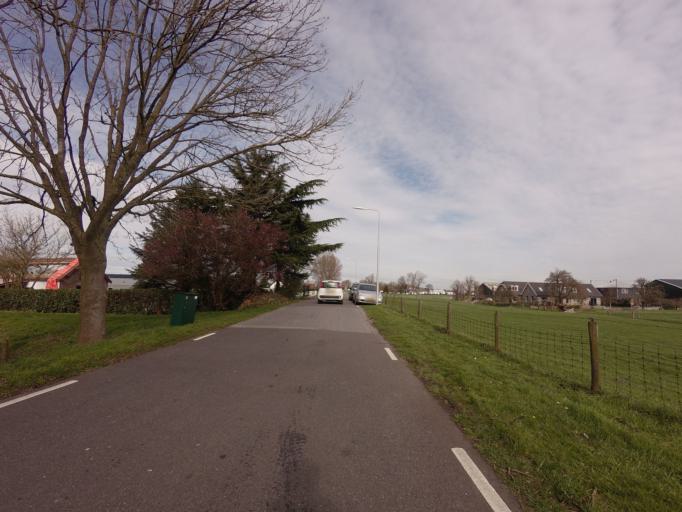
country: NL
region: North Holland
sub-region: Gemeente Uithoorn
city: Uithoorn
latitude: 52.2551
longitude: 4.8367
